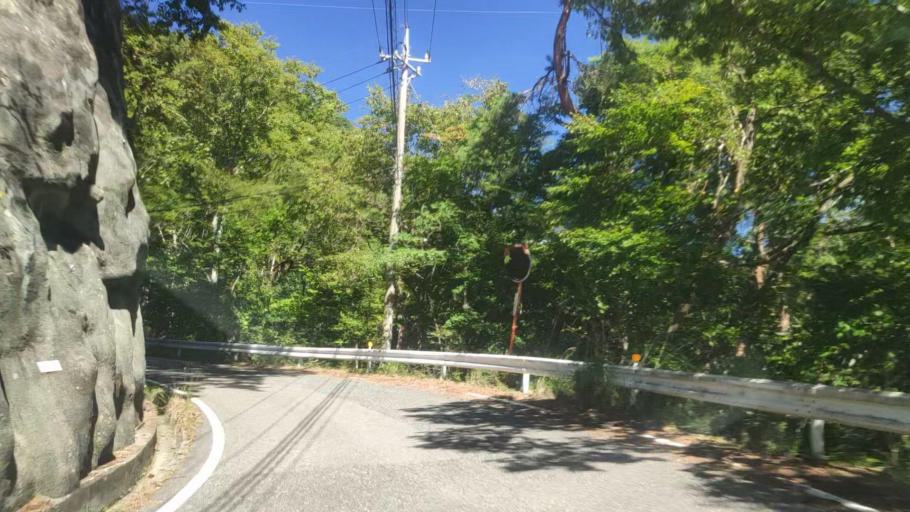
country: JP
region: Yamanashi
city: Fujikawaguchiko
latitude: 35.5493
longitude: 138.7772
